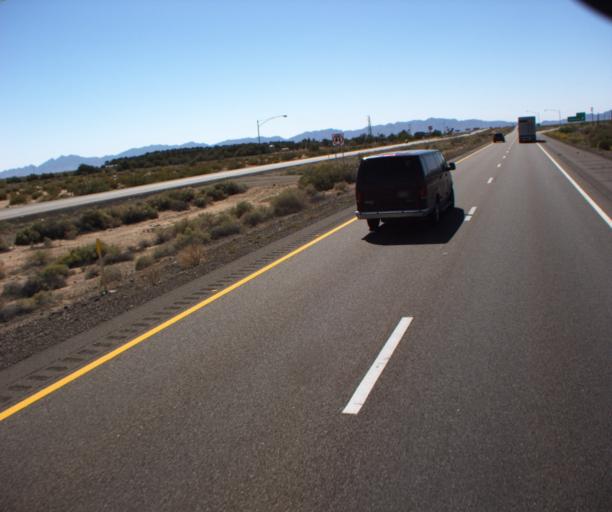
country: US
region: Arizona
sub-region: Yuma County
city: Wellton
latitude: 32.8035
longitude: -113.5336
